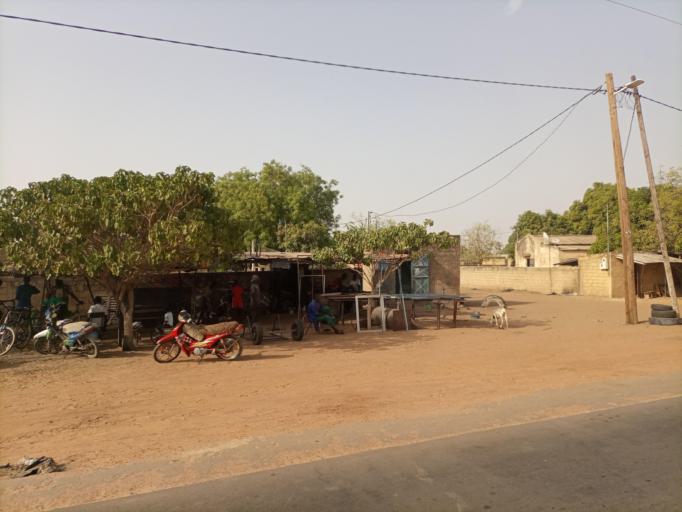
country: SN
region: Fatick
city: Foundiougne
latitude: 14.1214
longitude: -16.4349
